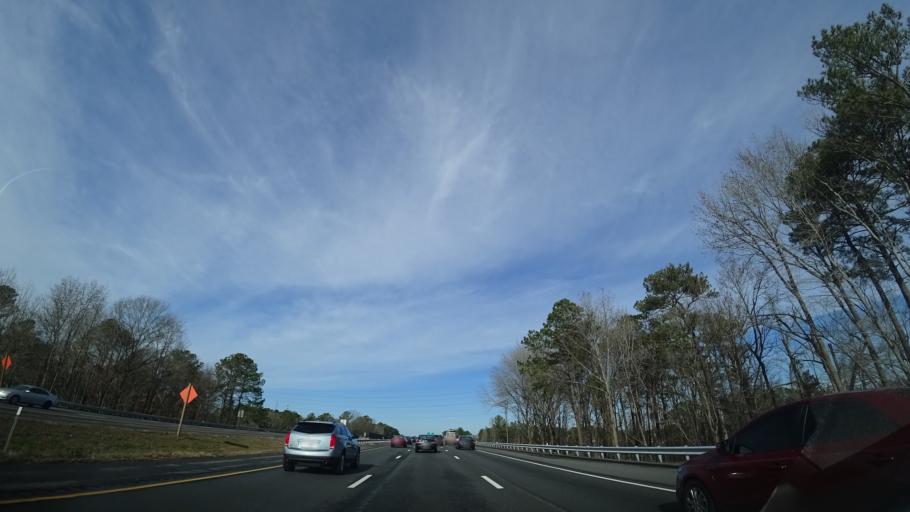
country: US
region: Virginia
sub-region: York County
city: Yorktown
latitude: 37.1611
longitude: -76.5417
